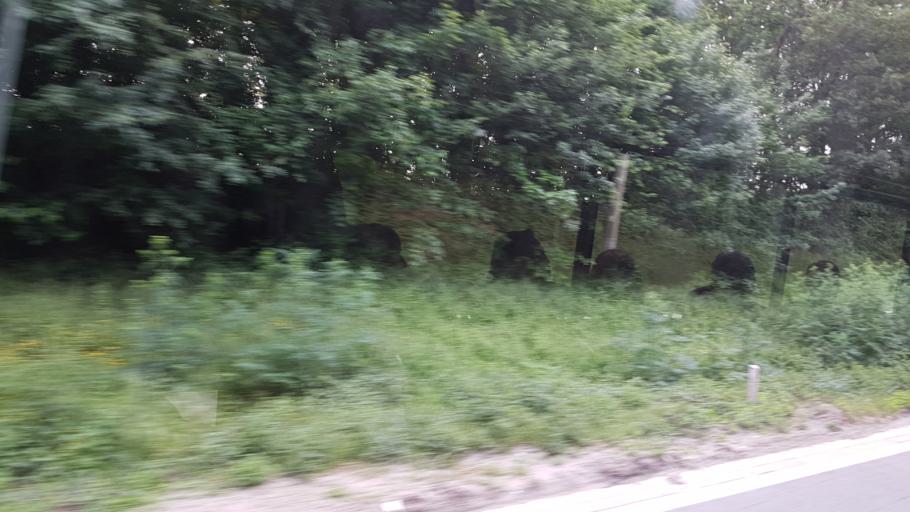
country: BE
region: Flanders
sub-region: Provincie Vlaams-Brabant
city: Kraainem
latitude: 50.8706
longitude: 4.4669
